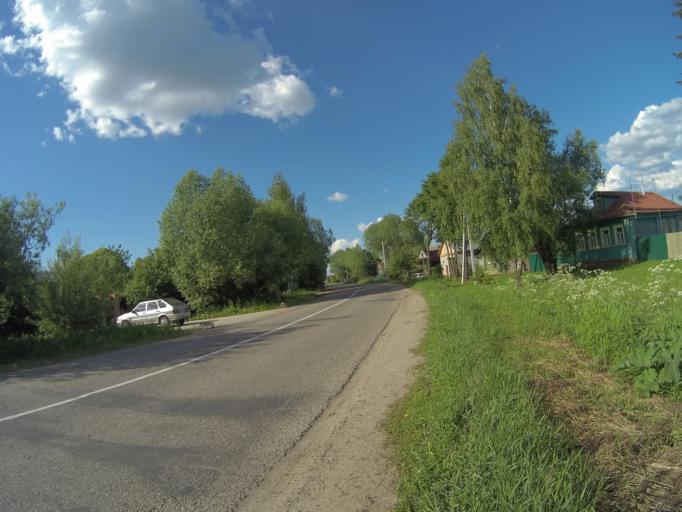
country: RU
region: Vladimir
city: Suzdal'
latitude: 56.4240
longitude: 40.4148
